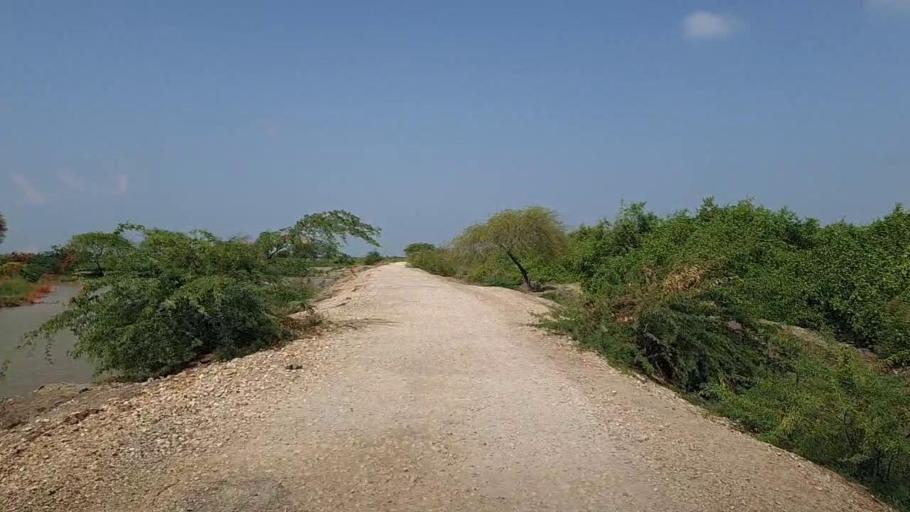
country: PK
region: Sindh
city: Mirpur Batoro
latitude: 24.6476
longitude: 68.4284
